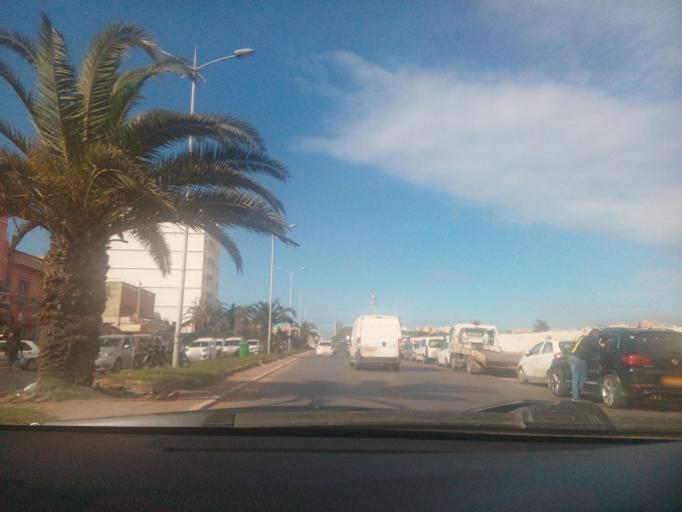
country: DZ
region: Oran
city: Oran
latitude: 35.6863
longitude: -0.6137
